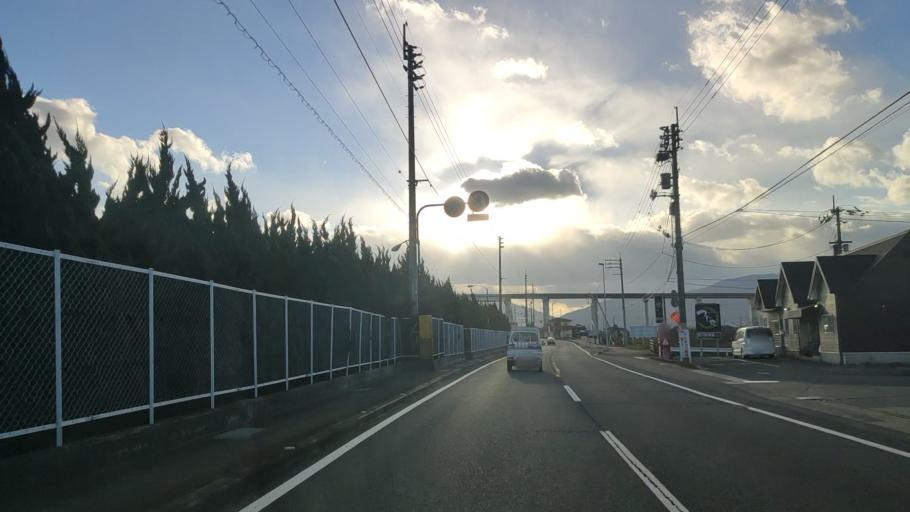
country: JP
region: Ehime
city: Saijo
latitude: 33.8916
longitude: 133.0899
